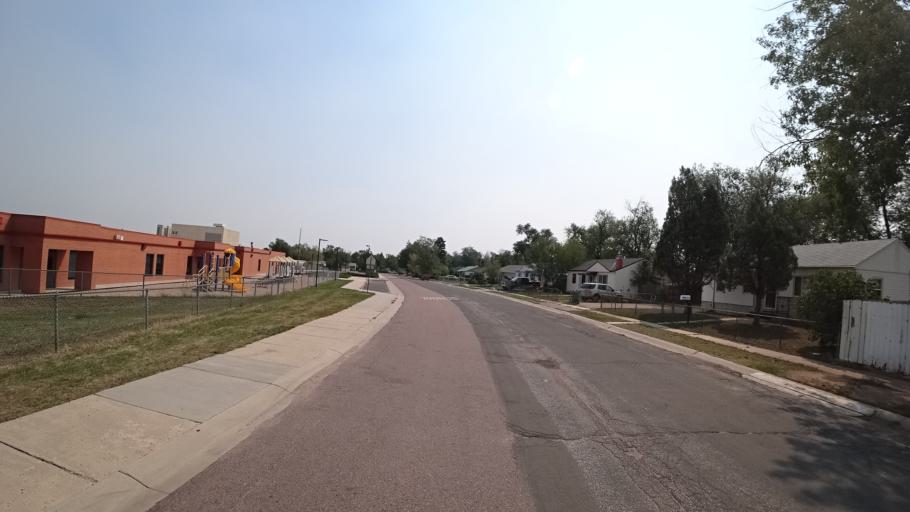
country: US
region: Colorado
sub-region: El Paso County
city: Colorado Springs
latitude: 38.8051
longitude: -104.8136
